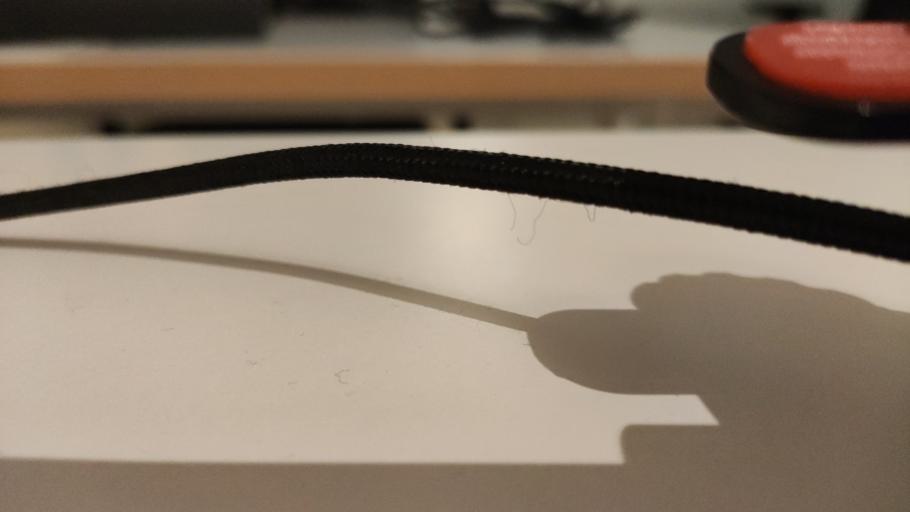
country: RU
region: Moskovskaya
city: Il'inskiy Pogost
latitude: 55.4936
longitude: 38.8747
